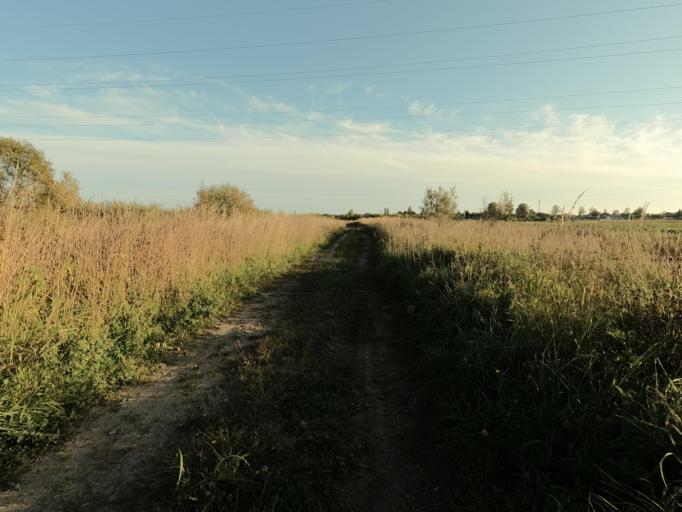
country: RU
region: Leningrad
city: Nikol'skoye
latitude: 59.7001
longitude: 30.7459
